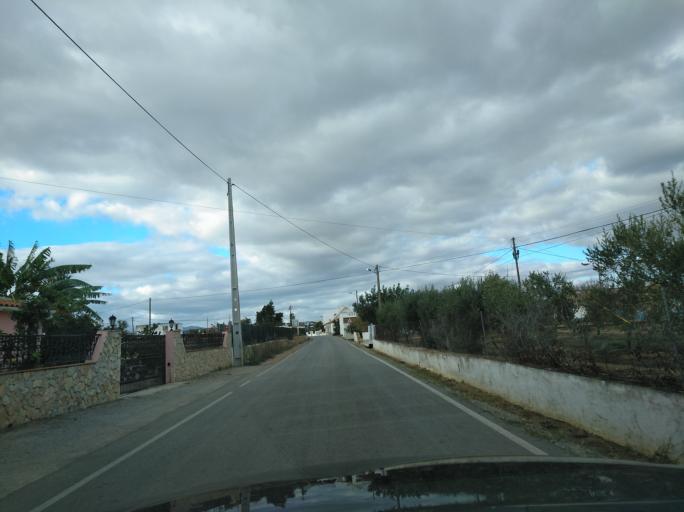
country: PT
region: Faro
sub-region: Tavira
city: Luz
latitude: 37.1003
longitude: -7.7075
